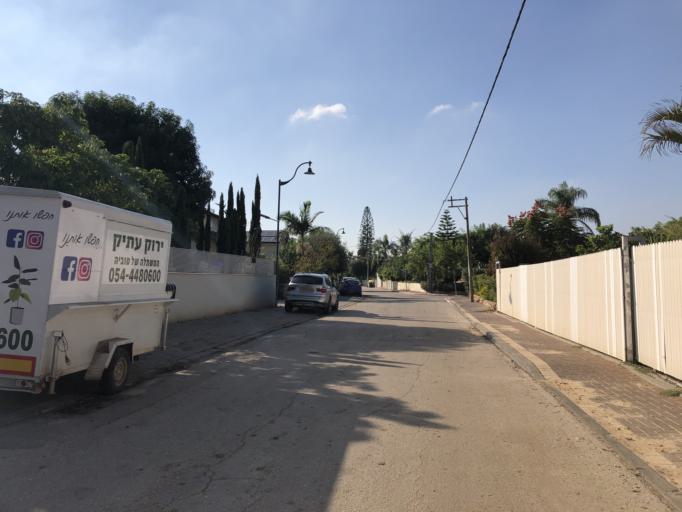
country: IL
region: Central District
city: Jaljulya
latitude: 32.1315
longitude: 34.9222
